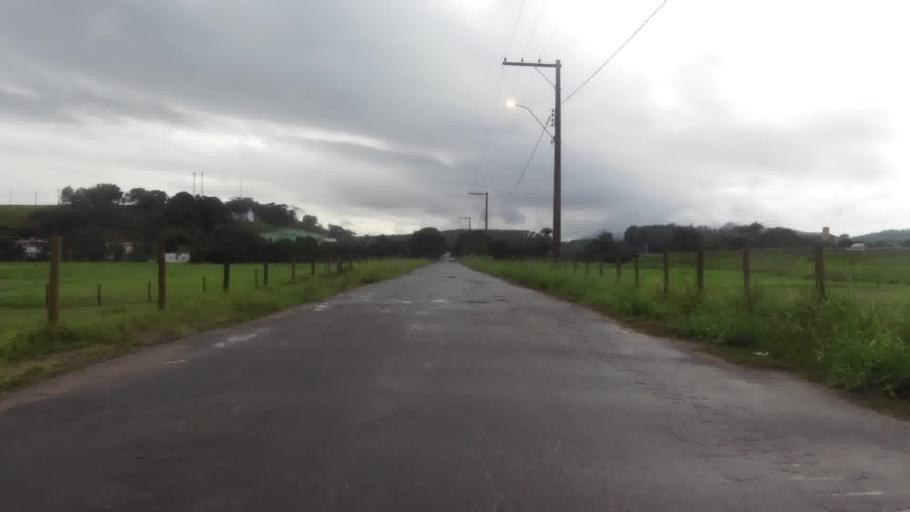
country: BR
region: Espirito Santo
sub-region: Alfredo Chaves
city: Alfredo Chaves
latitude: -20.6885
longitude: -40.6809
